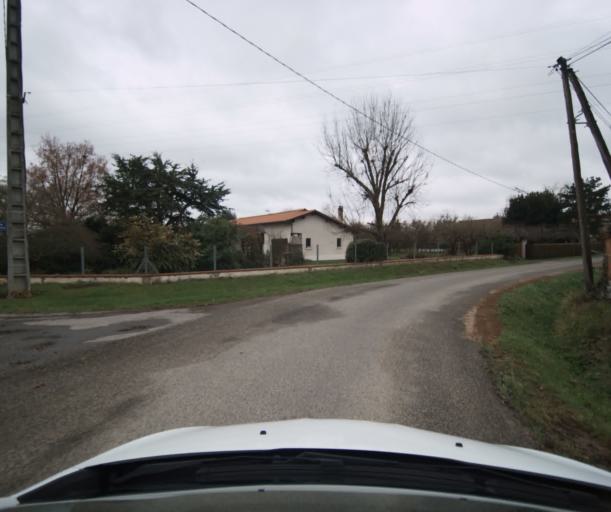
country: FR
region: Midi-Pyrenees
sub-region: Departement du Tarn-et-Garonne
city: Castelsarrasin
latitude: 44.0452
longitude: 1.1217
